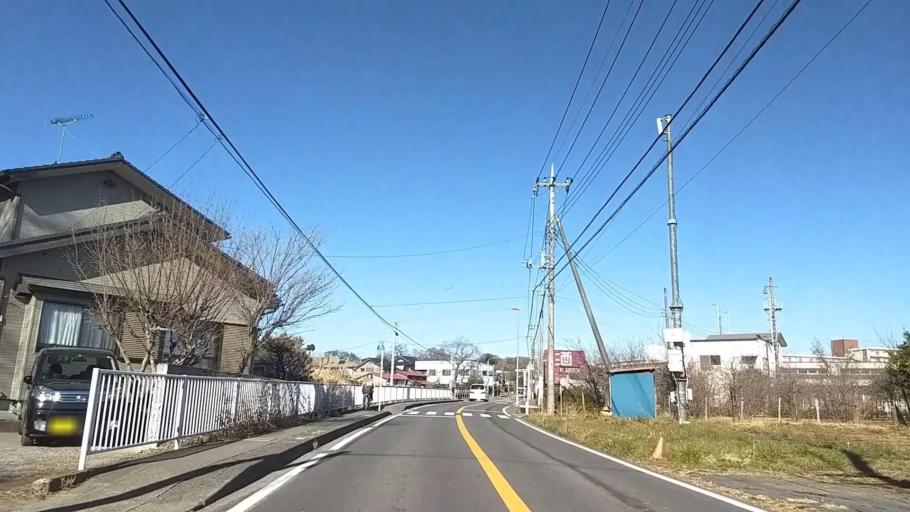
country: JP
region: Tokyo
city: Hachioji
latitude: 35.6046
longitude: 139.2989
